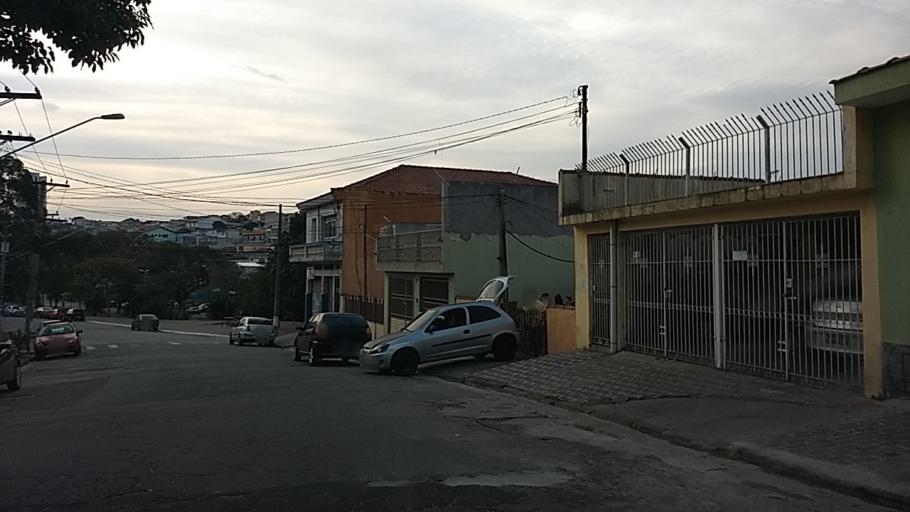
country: BR
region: Sao Paulo
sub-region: Guarulhos
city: Guarulhos
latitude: -23.5027
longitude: -46.5771
